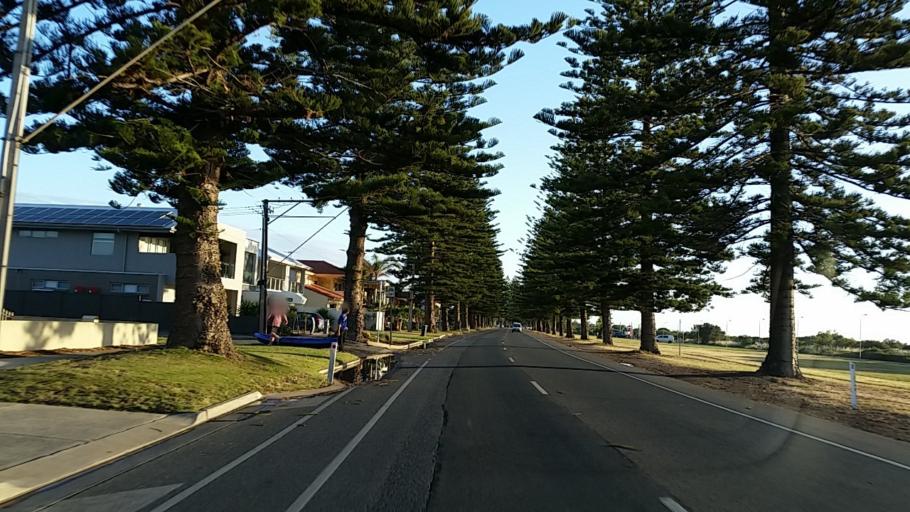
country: AU
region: South Australia
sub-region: Port Adelaide Enfield
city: Birkenhead
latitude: -34.7981
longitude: 138.4919
